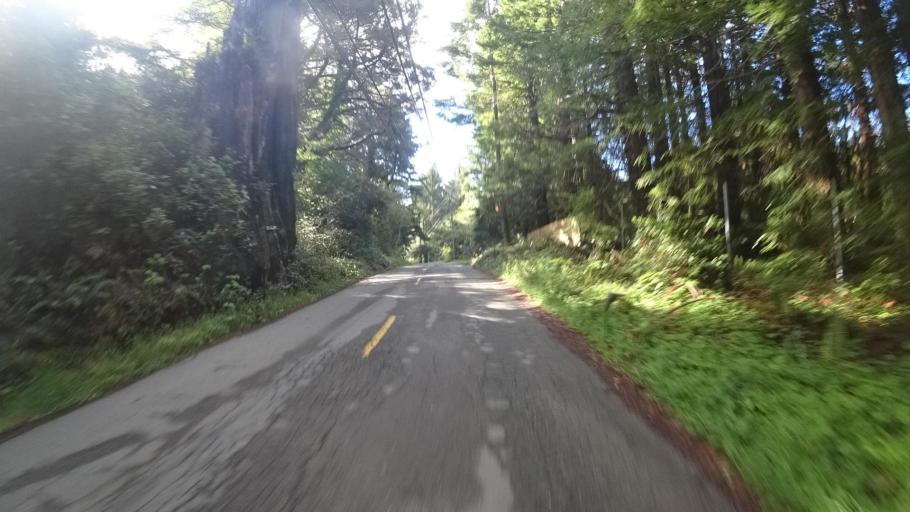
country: US
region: California
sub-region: Humboldt County
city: Westhaven-Moonstone
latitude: 41.0536
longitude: -124.1227
